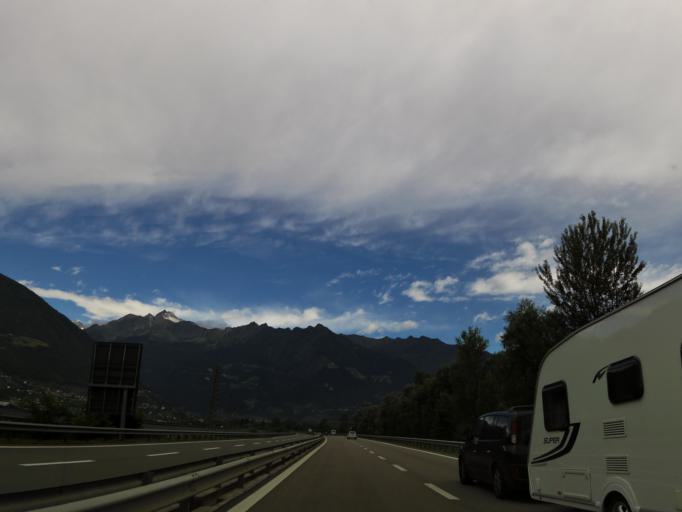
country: IT
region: Trentino-Alto Adige
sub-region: Bolzano
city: Sinigo
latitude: 46.6364
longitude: 11.1708
